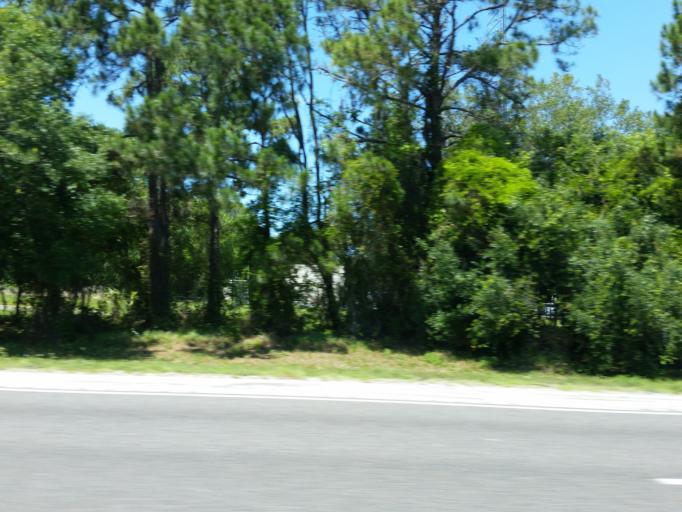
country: US
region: Florida
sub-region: Sarasota County
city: Fruitville
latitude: 27.3211
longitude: -82.4480
